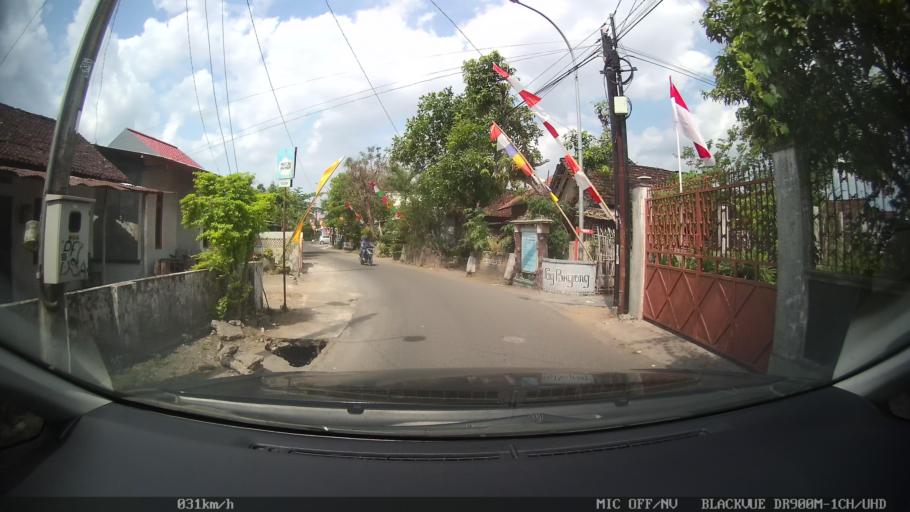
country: ID
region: Daerah Istimewa Yogyakarta
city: Gamping Lor
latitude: -7.8096
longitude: 110.3332
